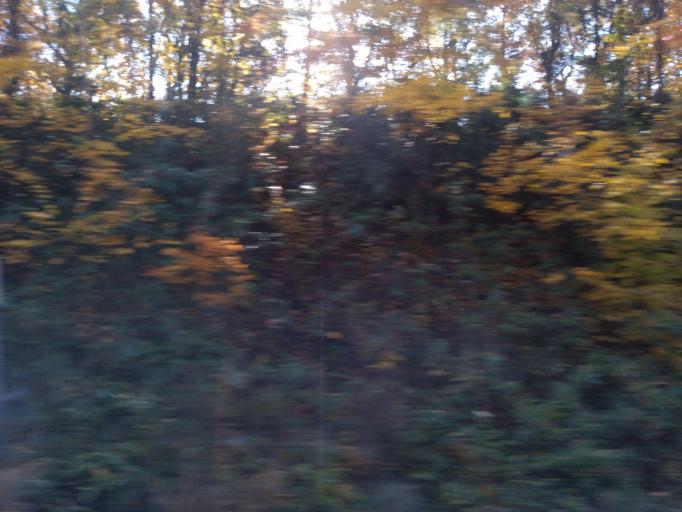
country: JP
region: Hokkaido
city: Kitahiroshima
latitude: 42.9957
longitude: 141.5385
